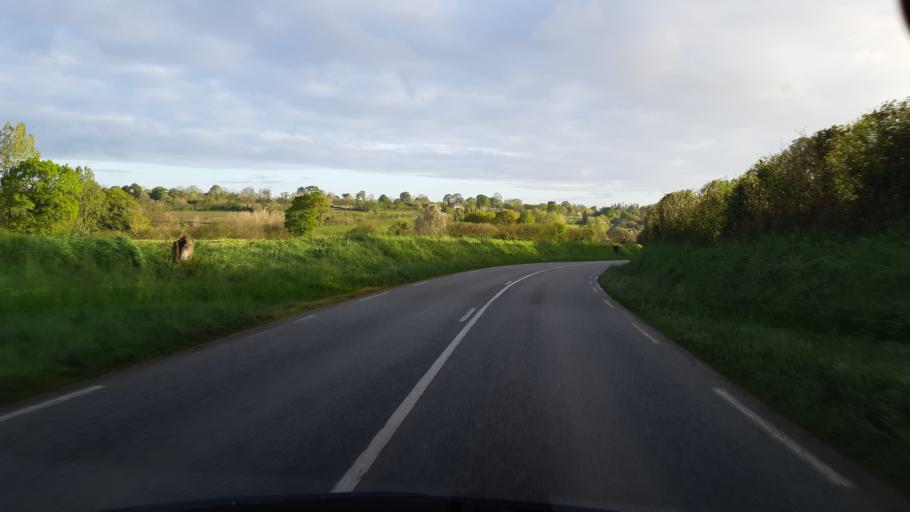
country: FR
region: Lower Normandy
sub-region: Departement de la Manche
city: Agneaux
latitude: 49.0650
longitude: -1.1325
